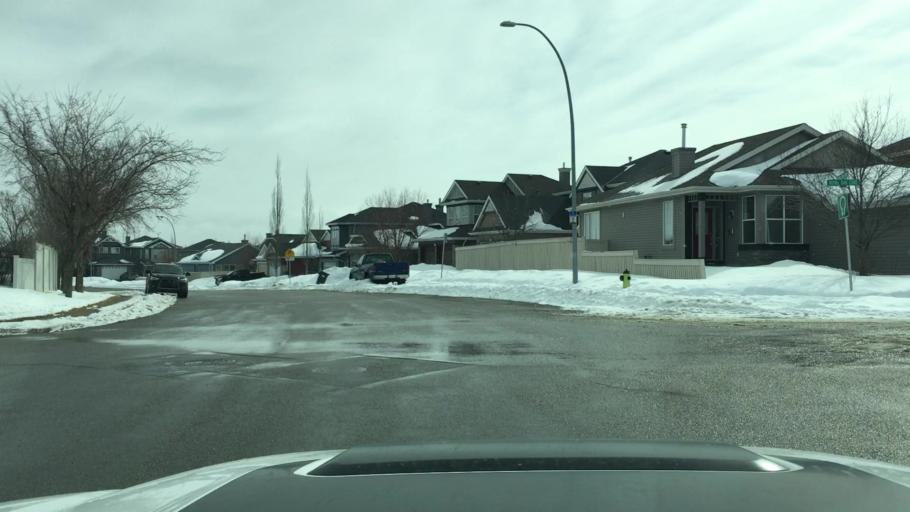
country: CA
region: Alberta
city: Calgary
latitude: 51.1477
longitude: -114.2313
